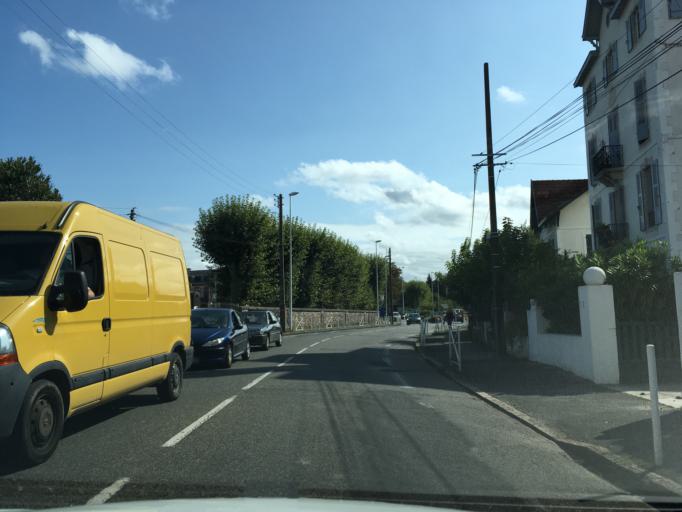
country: FR
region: Aquitaine
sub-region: Departement des Pyrenees-Atlantiques
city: Bayonne
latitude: 43.4834
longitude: -1.4825
